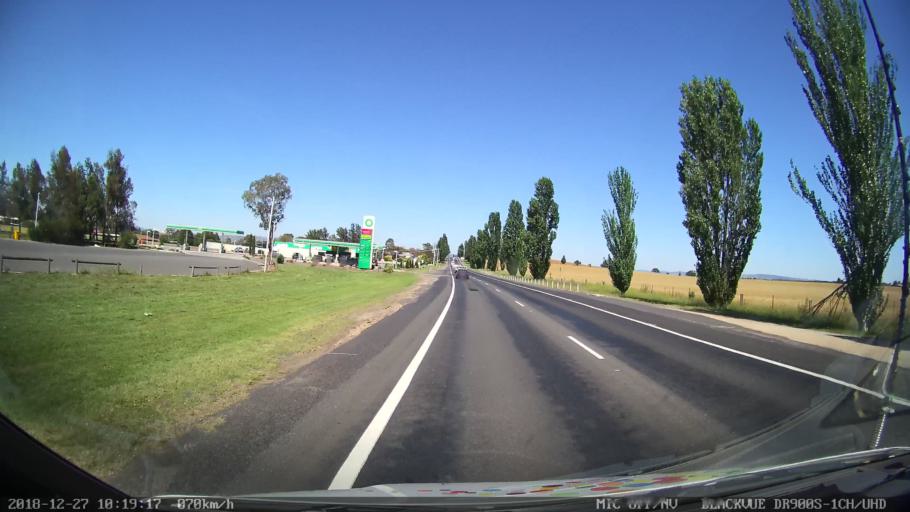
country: AU
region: New South Wales
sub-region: Bathurst Regional
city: Kelso
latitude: -33.4224
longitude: 149.6500
